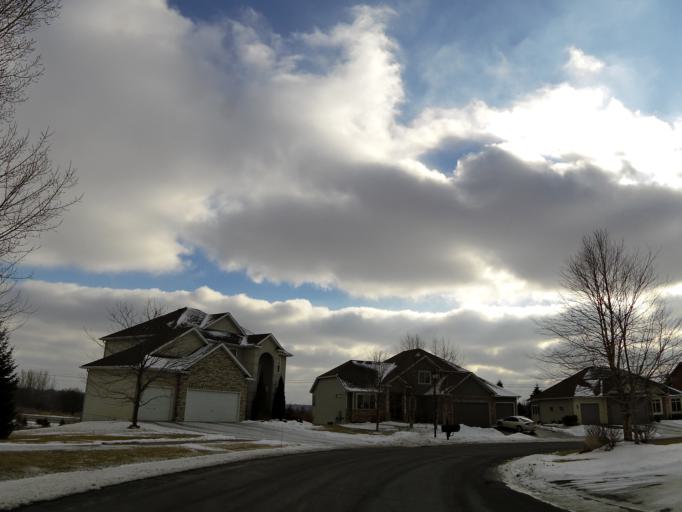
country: US
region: Minnesota
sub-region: Scott County
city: Prior Lake
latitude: 44.7261
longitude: -93.4619
